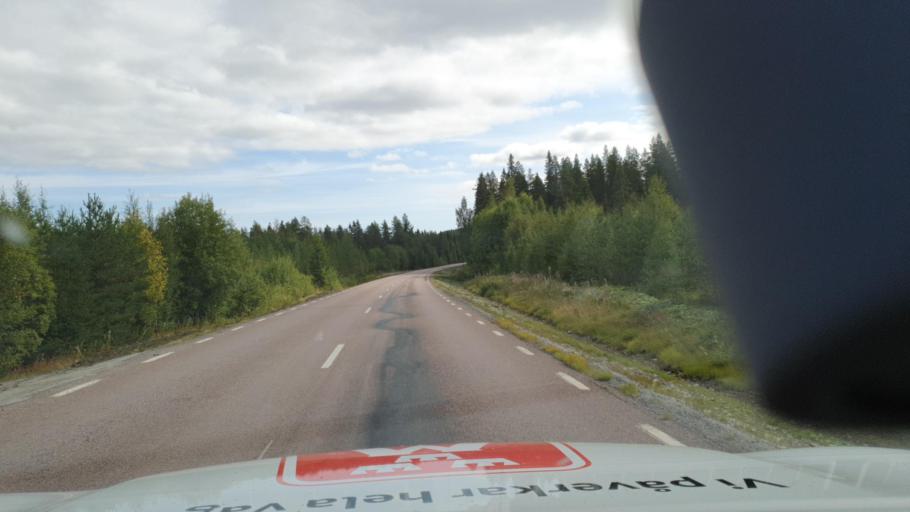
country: SE
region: Jaemtland
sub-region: Stroemsunds Kommun
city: Stroemsund
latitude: 63.7352
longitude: 15.7605
